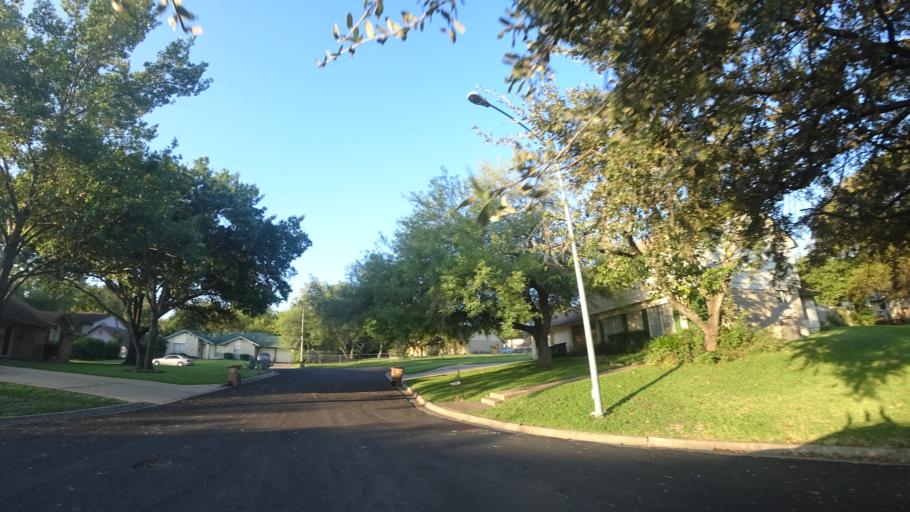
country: US
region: Texas
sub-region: Travis County
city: Austin
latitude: 30.3291
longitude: -97.6838
